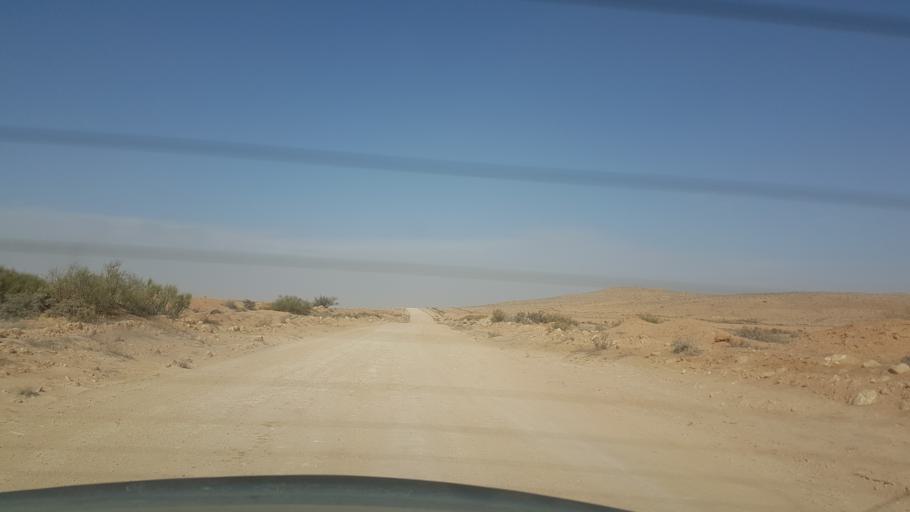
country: TN
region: Qabis
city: El Hamma
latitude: 33.6531
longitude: 9.7361
